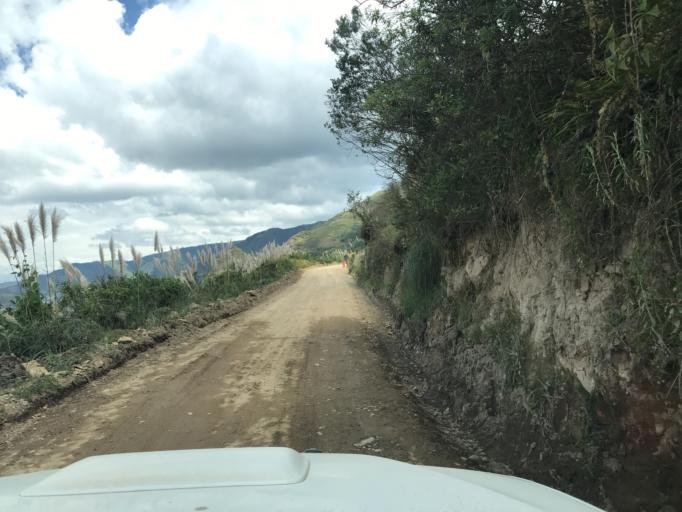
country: PE
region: Cajamarca
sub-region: Provincia de Chota
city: Querocoto
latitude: -6.3688
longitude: -79.0369
